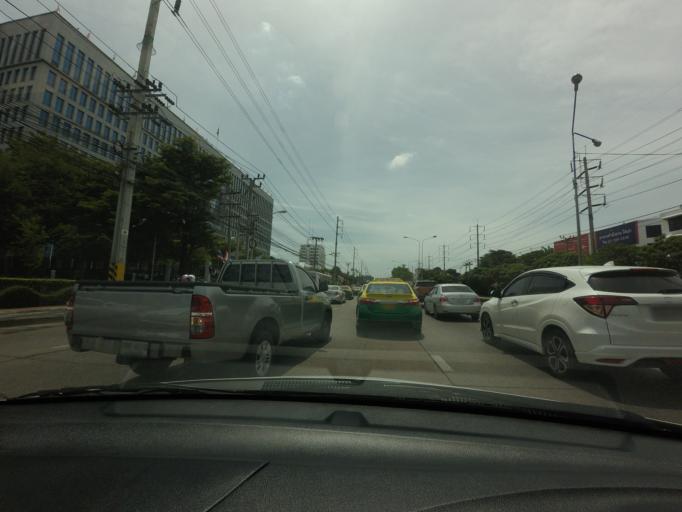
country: TH
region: Bangkok
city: Lak Si
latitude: 13.8899
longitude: 100.5693
